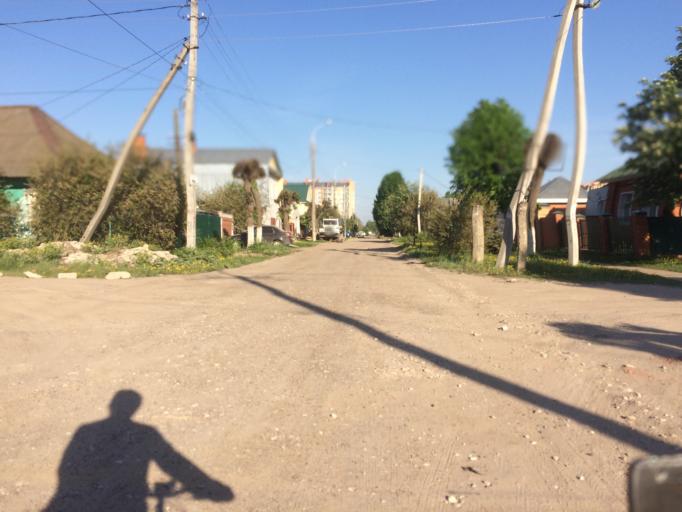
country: RU
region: Mariy-El
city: Medvedevo
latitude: 56.6479
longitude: 47.8423
